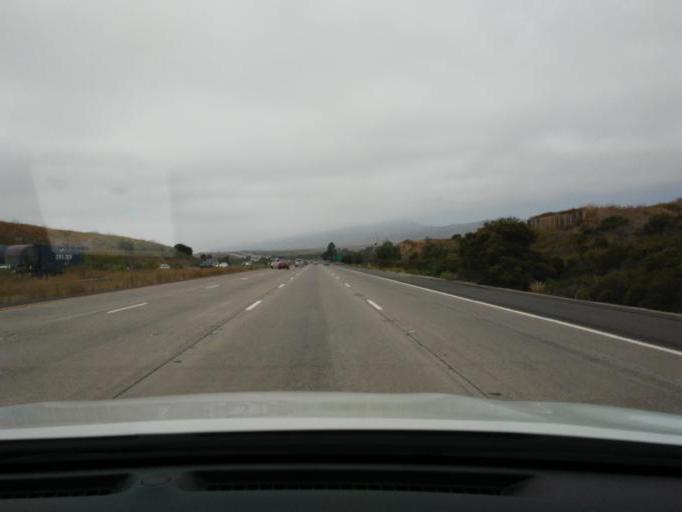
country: US
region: California
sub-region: San Diego County
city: Camp Pendleton South
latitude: 33.2886
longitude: -117.4545
